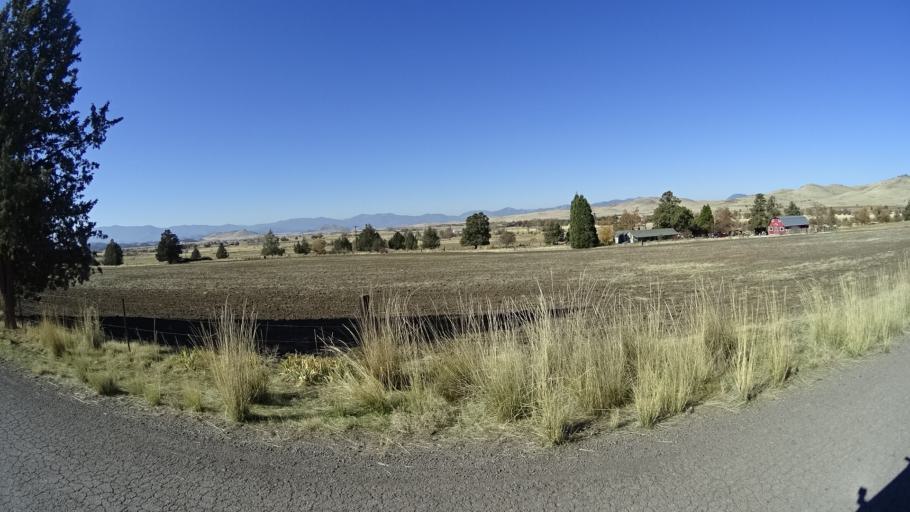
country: US
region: California
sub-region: Siskiyou County
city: Montague
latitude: 41.7164
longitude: -122.3725
